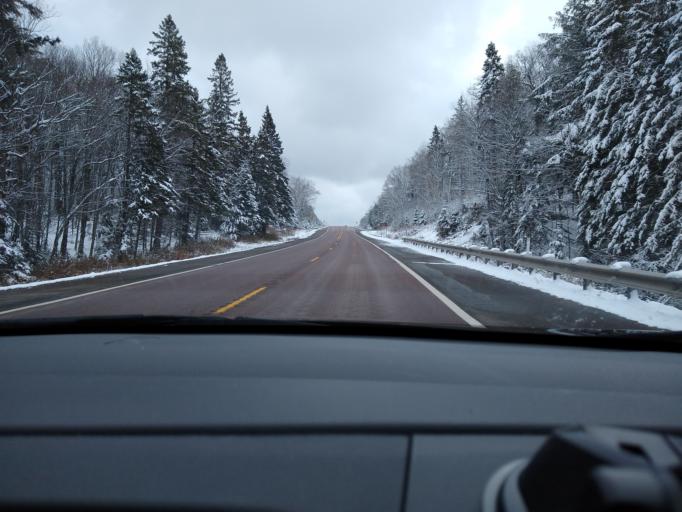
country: US
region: Wisconsin
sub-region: Vilas County
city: Eagle River
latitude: 46.2331
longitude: -89.0823
